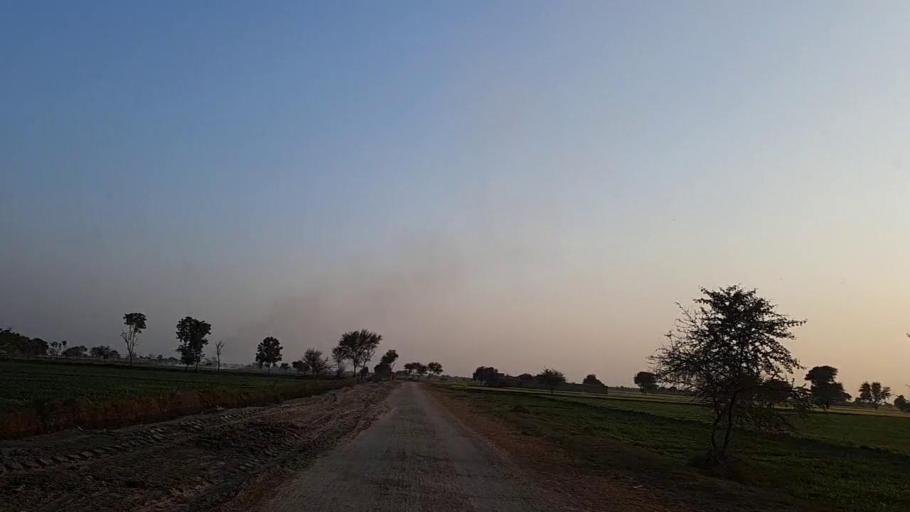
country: PK
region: Sindh
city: Shahdadpur
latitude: 25.9552
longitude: 68.5010
